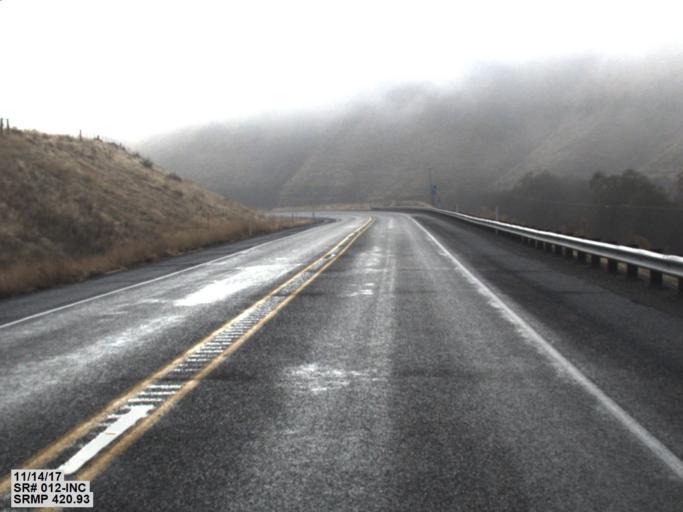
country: US
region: Washington
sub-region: Asotin County
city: Clarkston Heights-Vineland
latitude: 46.4205
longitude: -117.2847
